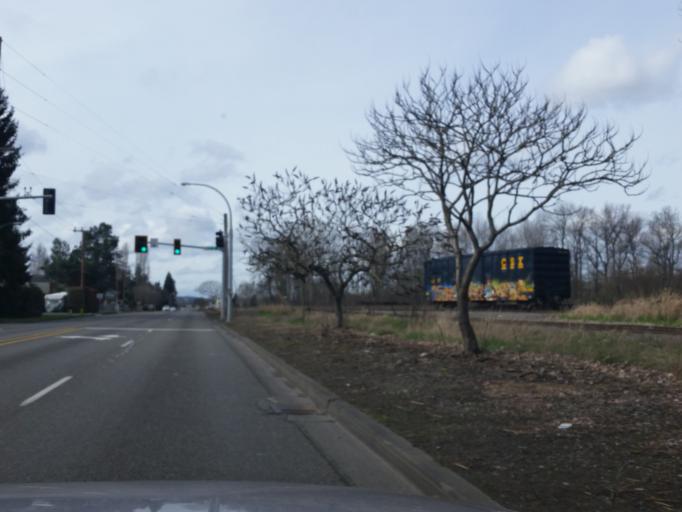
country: US
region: Washington
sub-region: Pierce County
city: North Puyallup
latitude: 47.1874
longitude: -122.2661
